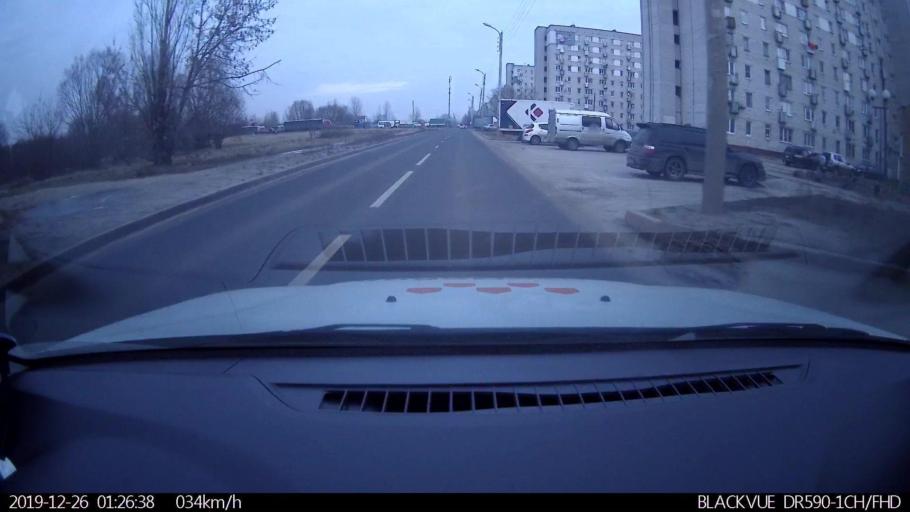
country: RU
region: Nizjnij Novgorod
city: Gorbatovka
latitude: 56.2697
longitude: 43.8681
